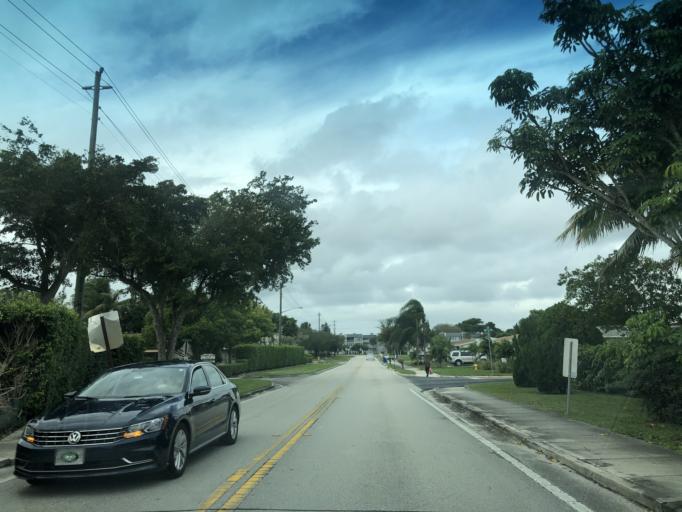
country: US
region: Florida
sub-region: Broward County
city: North Lauderdale
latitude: 26.2381
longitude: -80.2268
